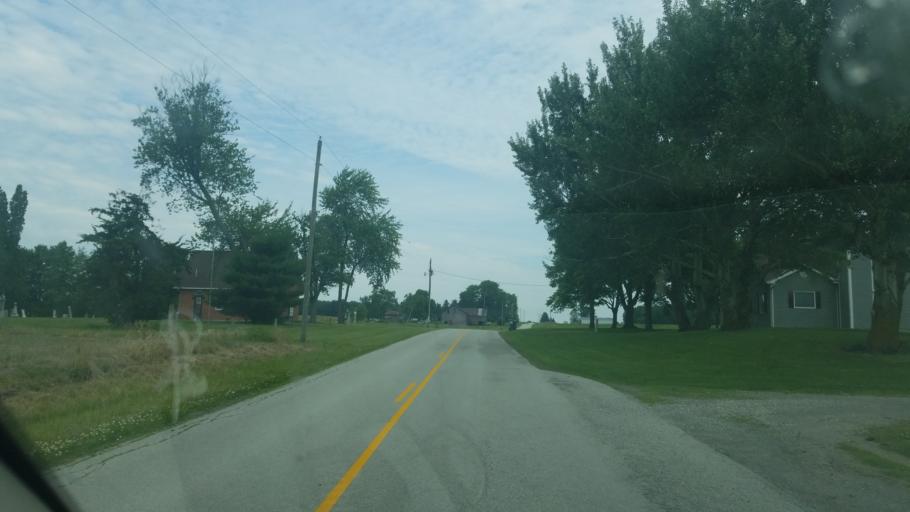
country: US
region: Ohio
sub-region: Wyandot County
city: Carey
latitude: 41.0349
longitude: -83.4399
